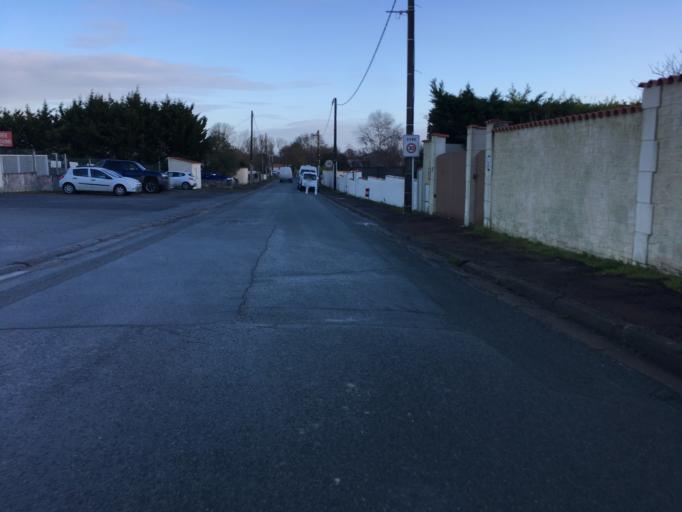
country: FR
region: Poitou-Charentes
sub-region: Departement de la Charente-Maritime
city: Nieul-sur-Mer
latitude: 46.2033
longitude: -1.1658
